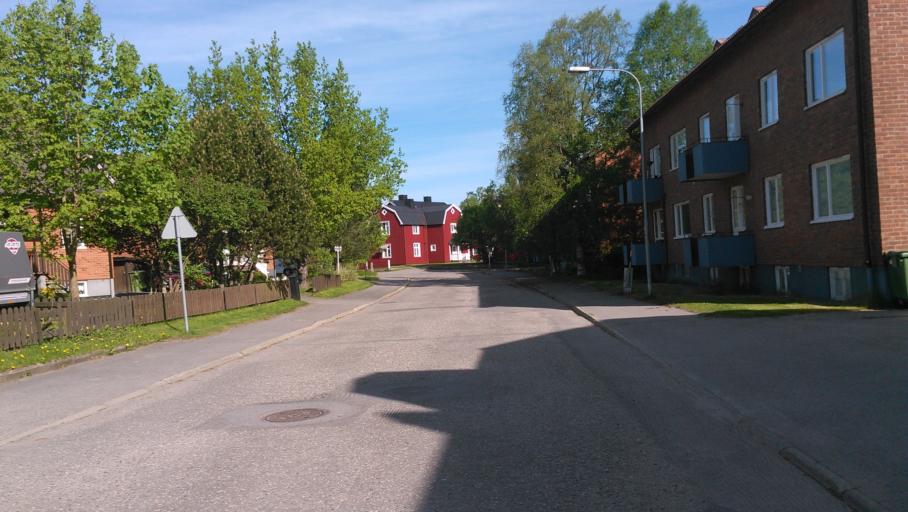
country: SE
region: Vaesterbotten
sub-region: Umea Kommun
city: Umea
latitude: 63.8109
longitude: 20.3017
